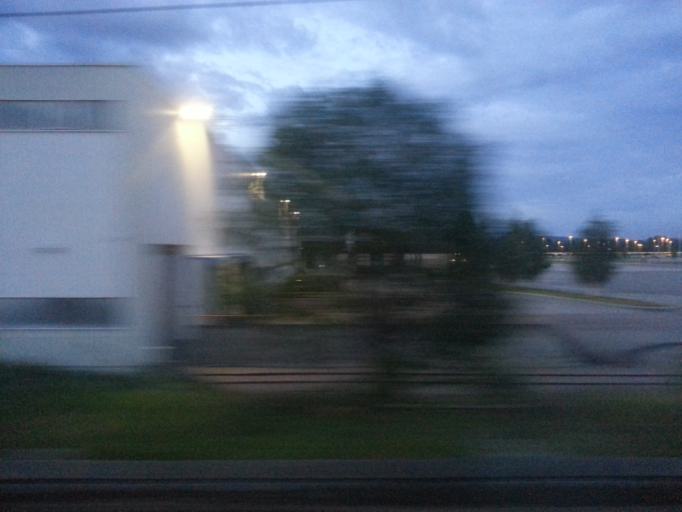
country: NO
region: Akershus
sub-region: Skedsmo
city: Lillestrom
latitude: 59.9690
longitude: 11.0682
